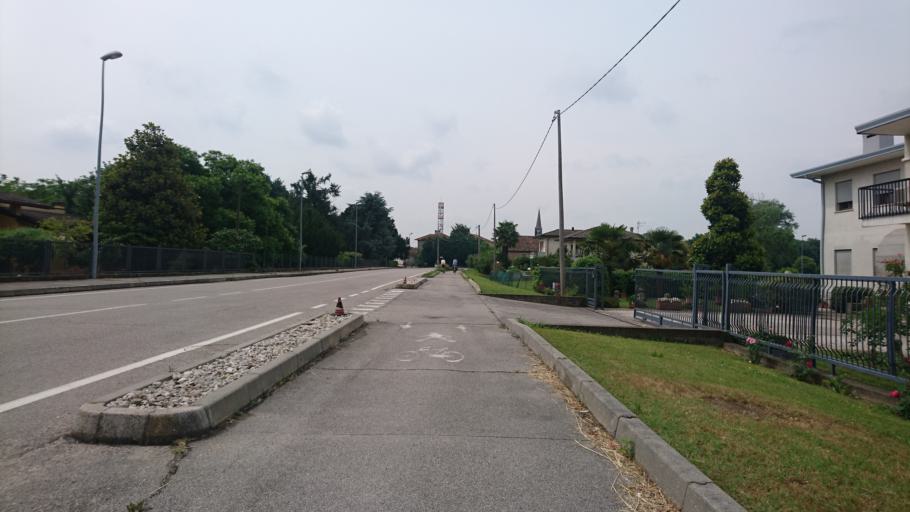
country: IT
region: Veneto
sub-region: Provincia di Rovigo
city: Lendinara
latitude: 45.1152
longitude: 11.6209
